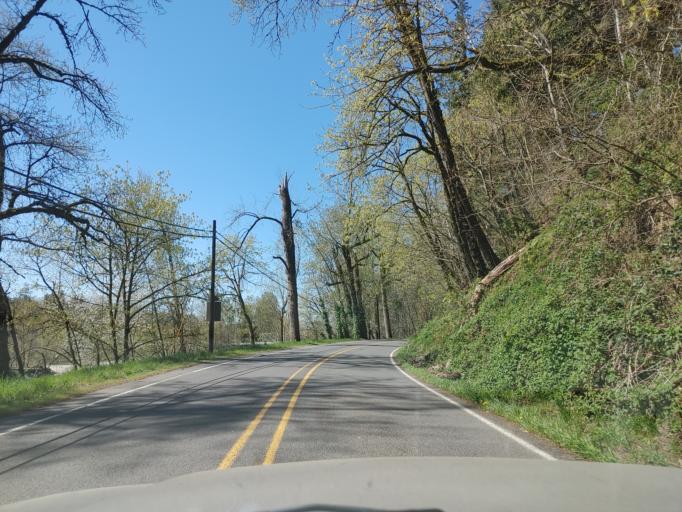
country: US
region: Oregon
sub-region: Multnomah County
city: Troutdale
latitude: 45.5369
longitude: -122.3735
